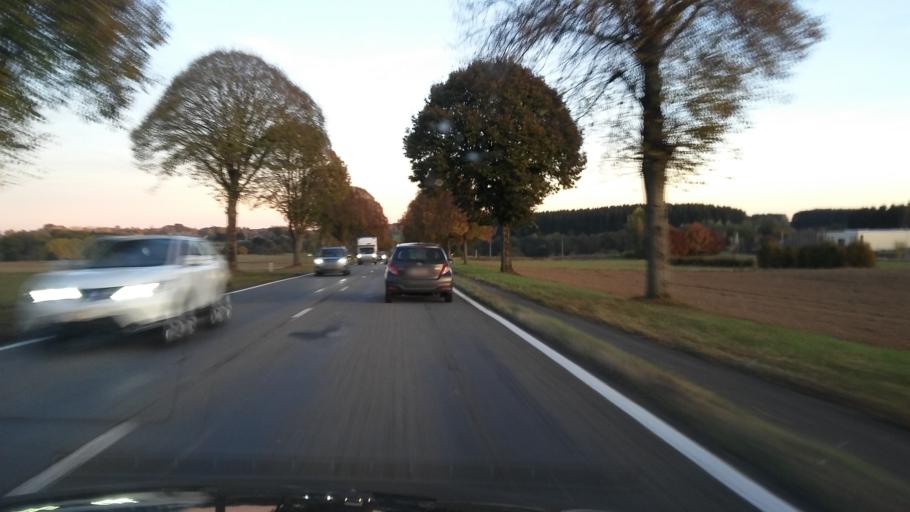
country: BE
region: Wallonia
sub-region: Province du Luxembourg
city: Florenville
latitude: 49.6905
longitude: 5.3402
